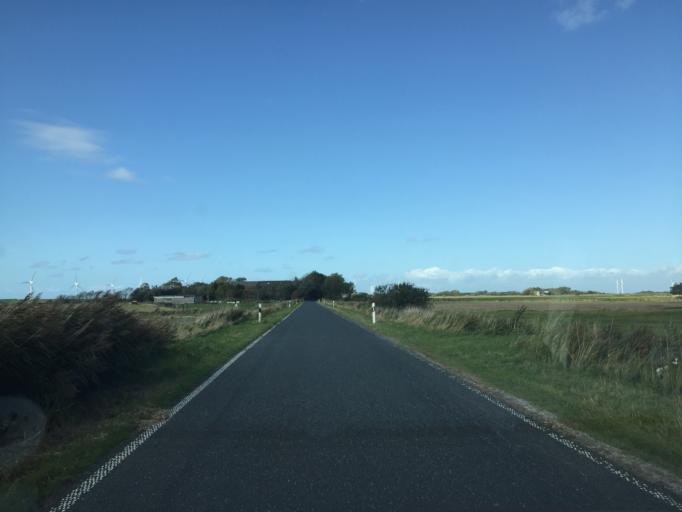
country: DE
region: Schleswig-Holstein
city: Emmelsbull-Horsbull
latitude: 54.8140
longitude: 8.6524
